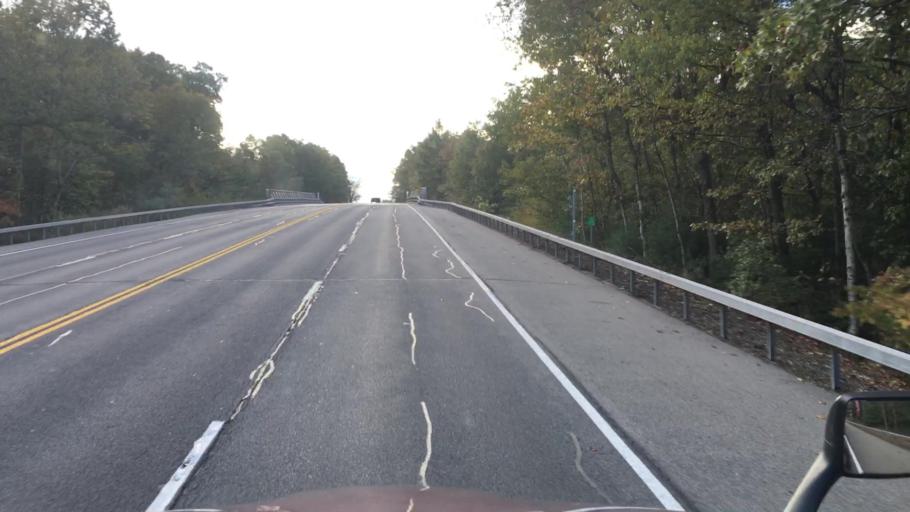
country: US
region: New York
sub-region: Saratoga County
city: Milton
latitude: 43.0439
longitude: -73.8175
